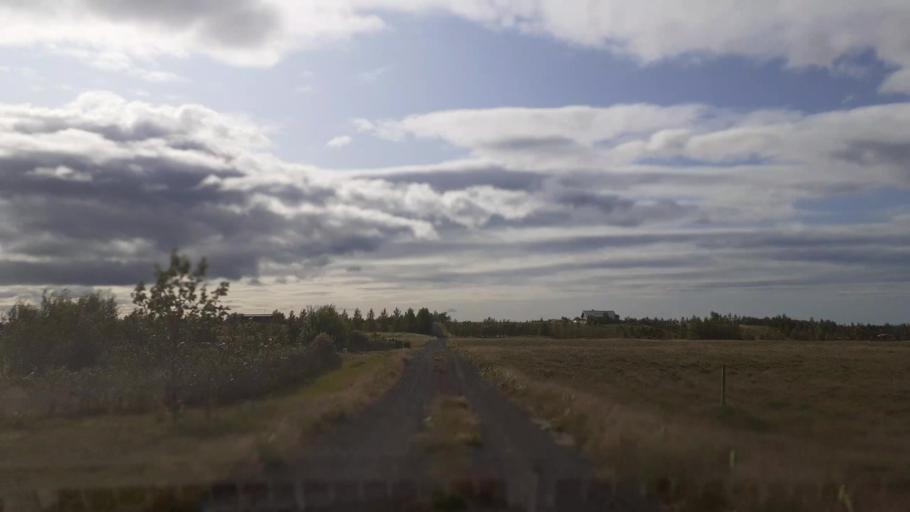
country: IS
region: South
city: Vestmannaeyjar
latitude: 63.7721
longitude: -20.2982
